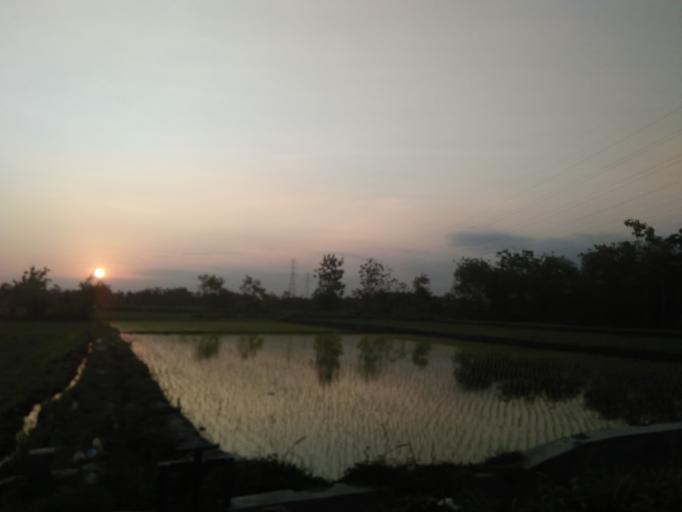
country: ID
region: Daerah Istimewa Yogyakarta
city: Sewon
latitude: -7.8524
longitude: 110.4099
